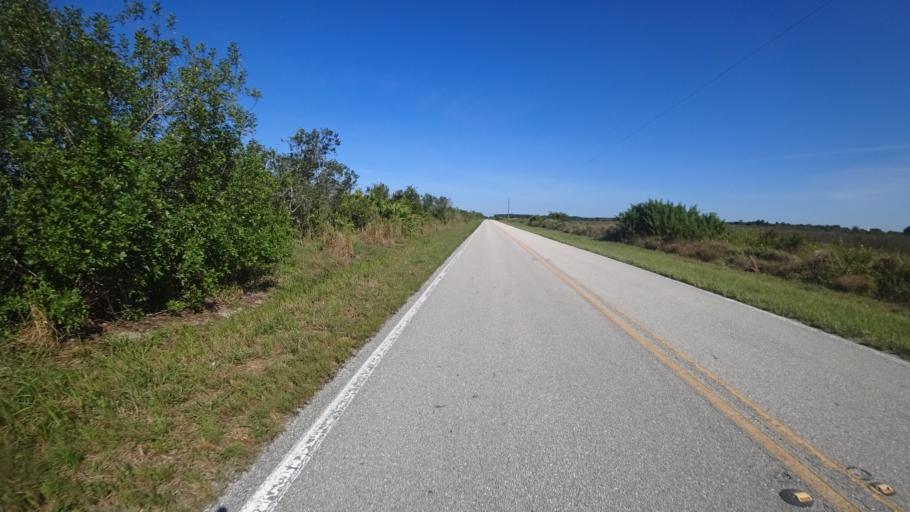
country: US
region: Florida
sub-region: Hillsborough County
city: Wimauma
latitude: 27.6057
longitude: -82.2928
